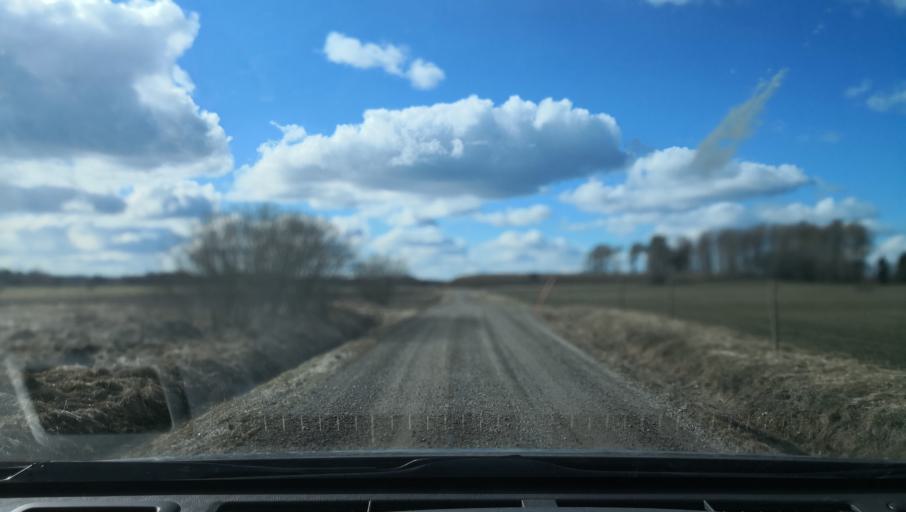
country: SE
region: OErebro
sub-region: Lindesbergs Kommun
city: Fellingsbro
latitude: 59.4122
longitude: 15.6741
